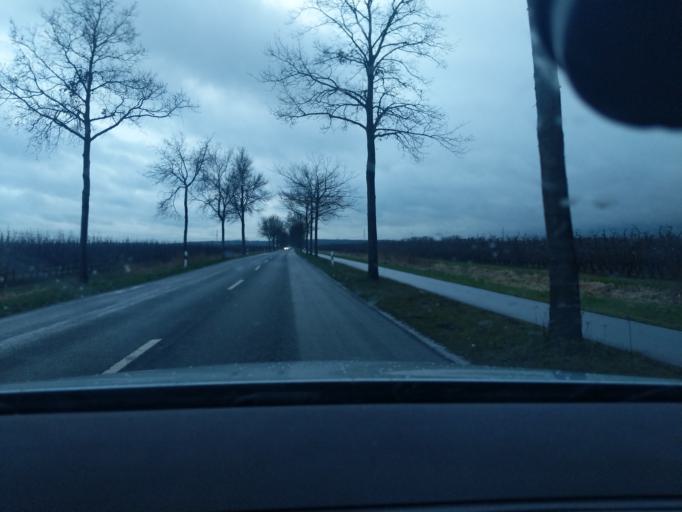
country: DE
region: Lower Saxony
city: Jork
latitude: 53.5134
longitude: 9.6678
